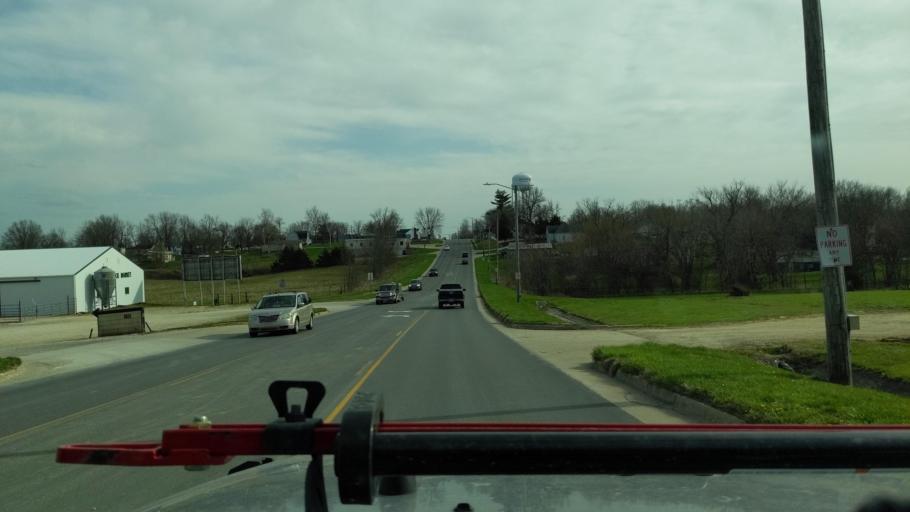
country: US
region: Missouri
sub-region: Macon County
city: Macon
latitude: 39.7351
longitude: -92.4655
